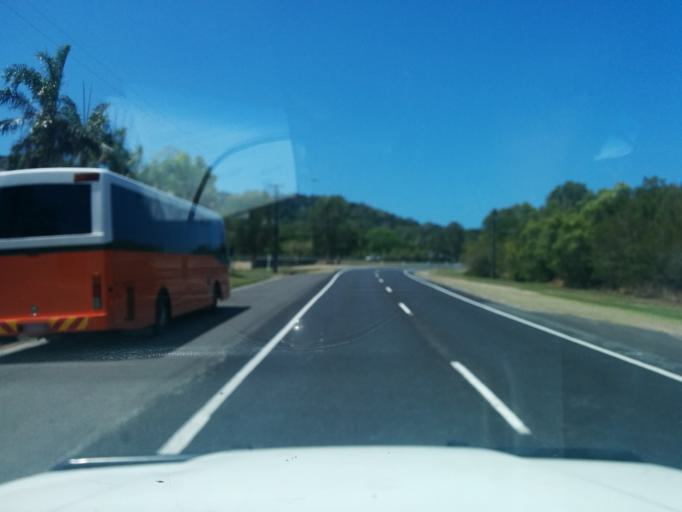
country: AU
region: Queensland
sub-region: Cairns
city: Cairns
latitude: -16.9057
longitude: 145.7506
